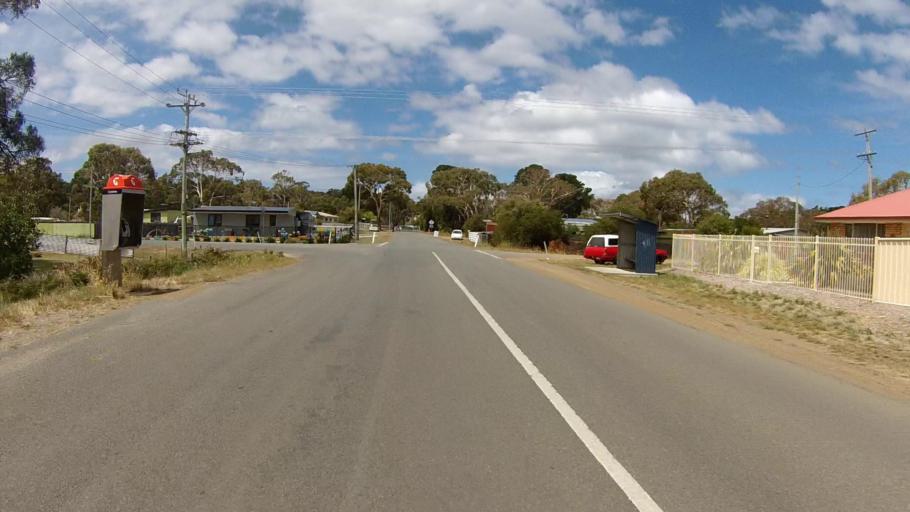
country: AU
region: Tasmania
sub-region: Sorell
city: Sorell
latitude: -42.8706
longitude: 147.6384
